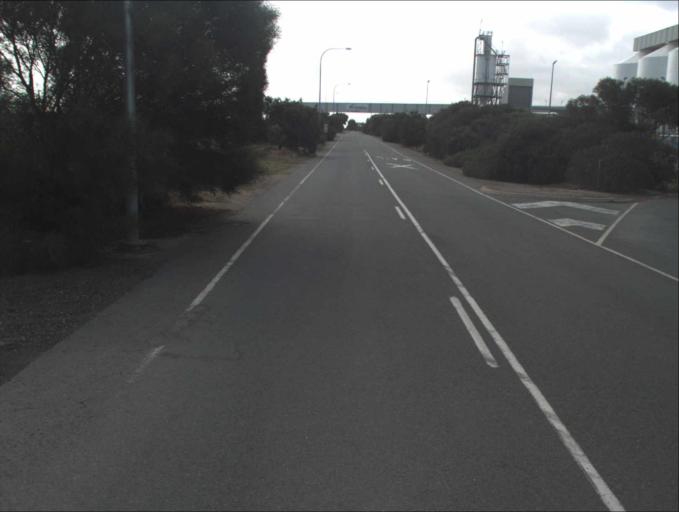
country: AU
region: South Australia
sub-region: Port Adelaide Enfield
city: Birkenhead
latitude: -34.7723
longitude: 138.5015
